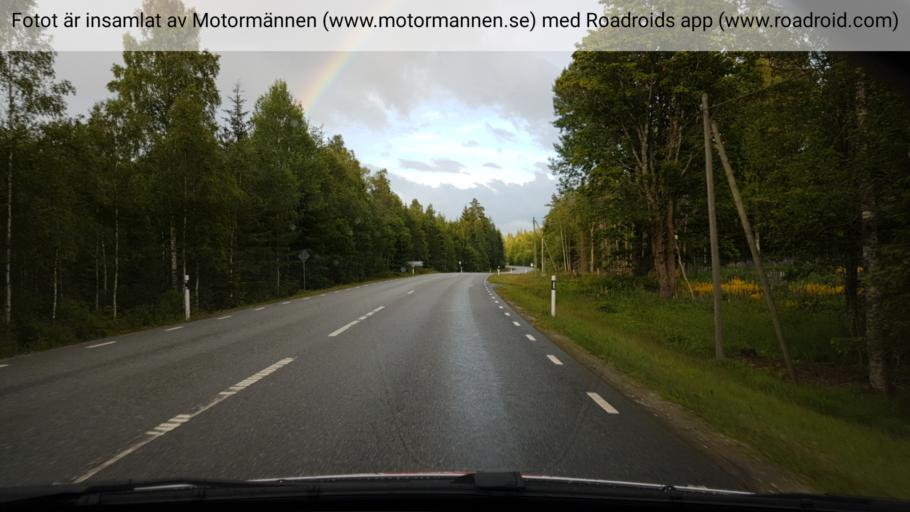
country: SE
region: OErebro
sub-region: Nora Kommun
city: As
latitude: 59.5189
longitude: 14.9254
